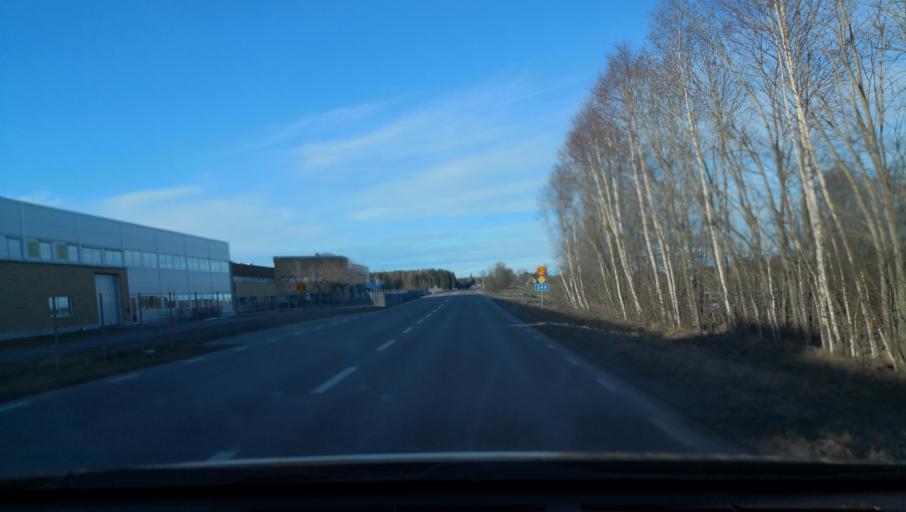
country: SE
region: Uppsala
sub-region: Osthammars Kommun
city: Gimo
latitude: 60.1793
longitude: 18.1905
